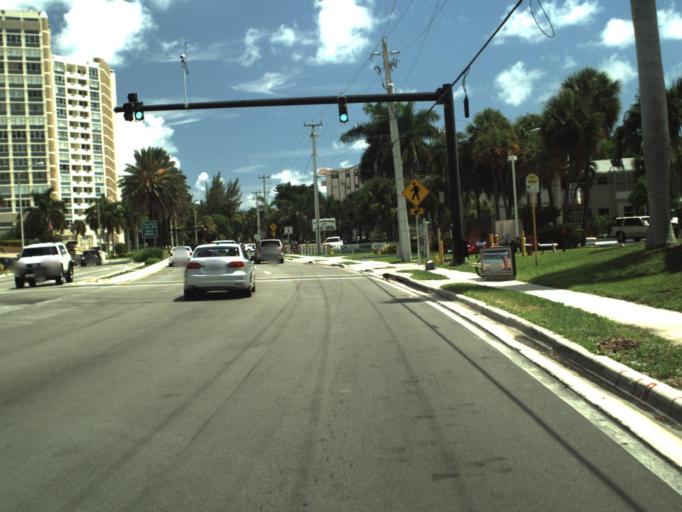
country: US
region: Florida
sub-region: Miami-Dade County
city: Sunny Isles Beach
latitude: 25.9776
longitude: -80.1203
